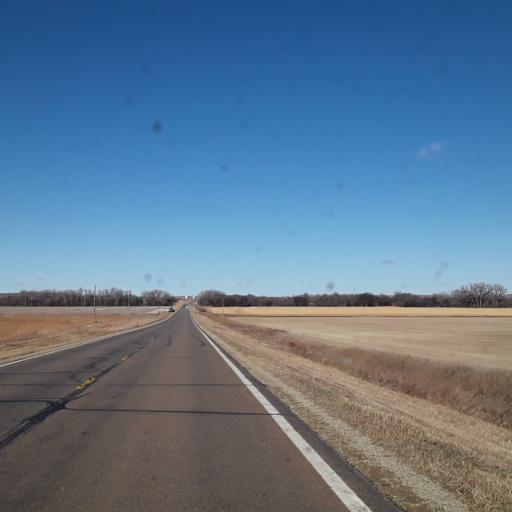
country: US
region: Kansas
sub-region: Lincoln County
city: Lincoln
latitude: 38.9975
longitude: -98.1513
